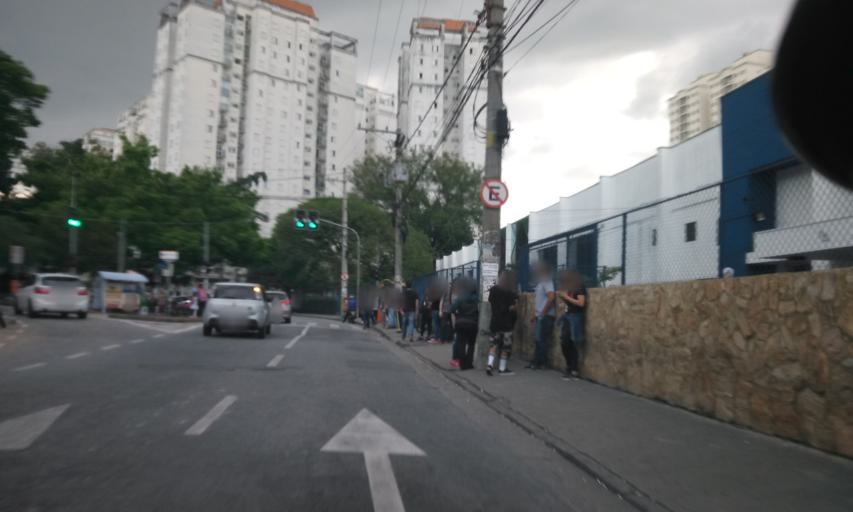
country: BR
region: Sao Paulo
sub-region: Sao Bernardo Do Campo
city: Sao Bernardo do Campo
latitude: -23.7013
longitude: -46.5481
